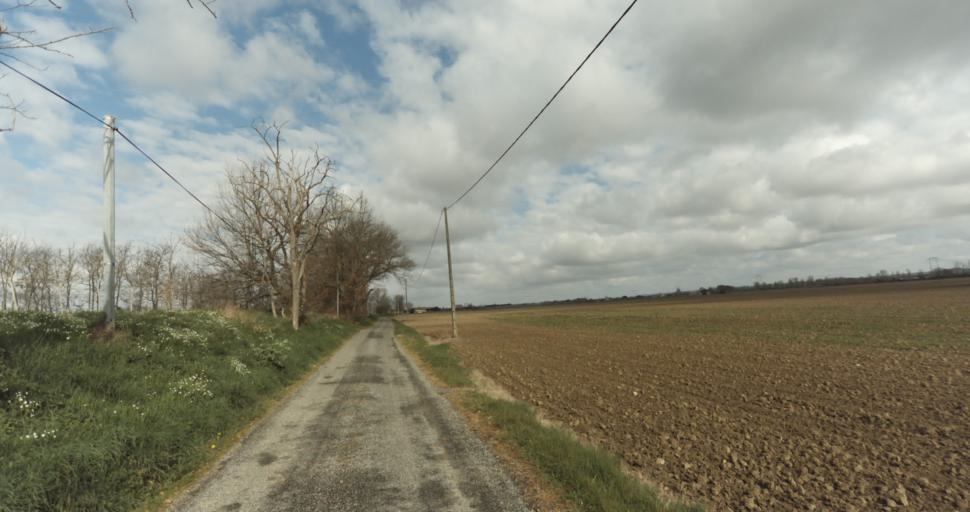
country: FR
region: Midi-Pyrenees
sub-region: Departement de la Haute-Garonne
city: Auterive
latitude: 43.3467
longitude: 1.4442
